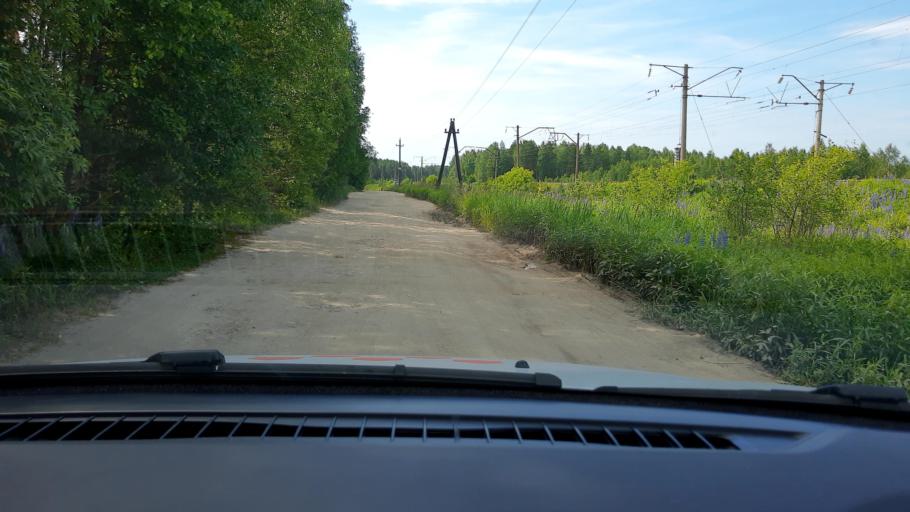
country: RU
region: Nizjnij Novgorod
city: Linda
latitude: 56.6657
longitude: 44.1684
